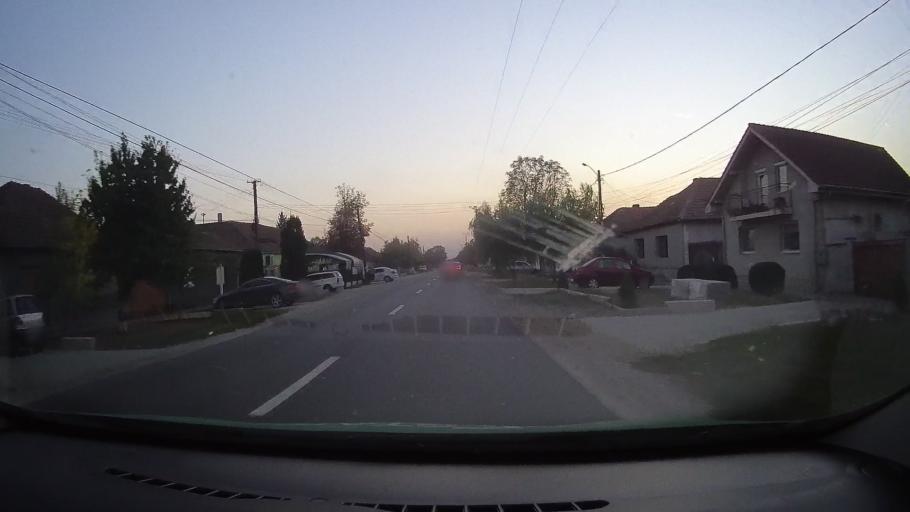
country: RO
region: Arad
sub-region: Comuna Zimandu Nou
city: Zimandu Nou
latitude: 46.2805
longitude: 21.3981
